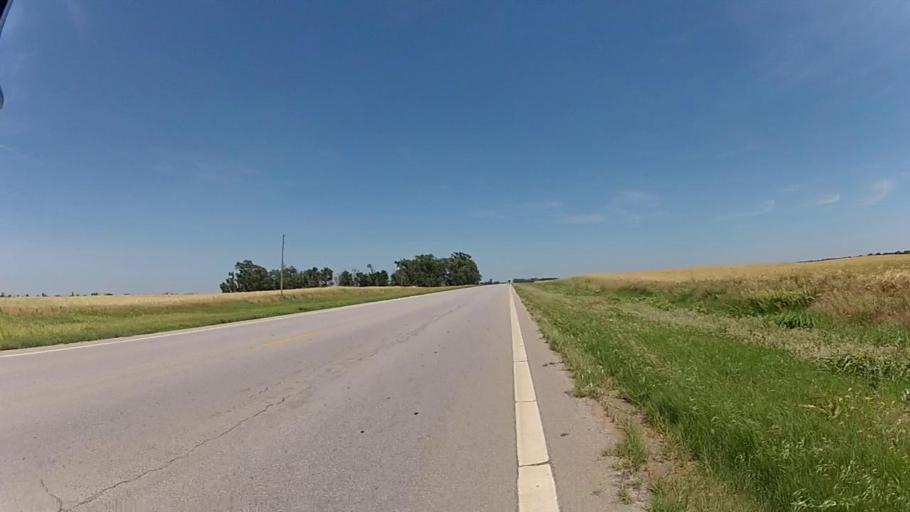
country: US
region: Kansas
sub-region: Harper County
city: Harper
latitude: 37.2386
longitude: -98.1115
